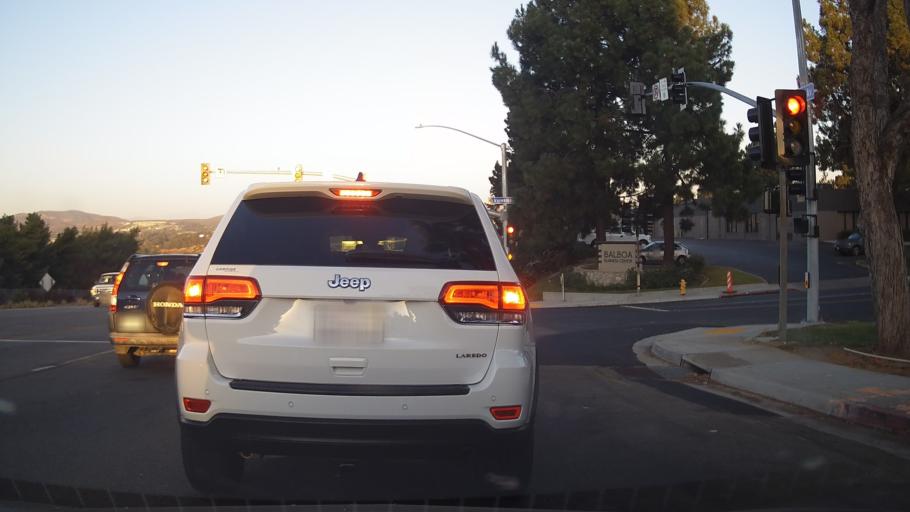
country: US
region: California
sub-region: San Diego County
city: San Diego
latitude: 32.8246
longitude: -117.1246
